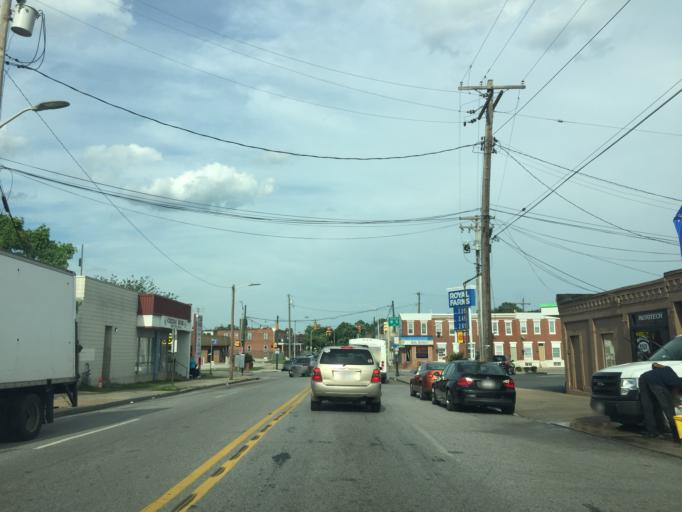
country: US
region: Maryland
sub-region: City of Baltimore
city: Baltimore
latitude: 39.2949
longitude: -76.5704
